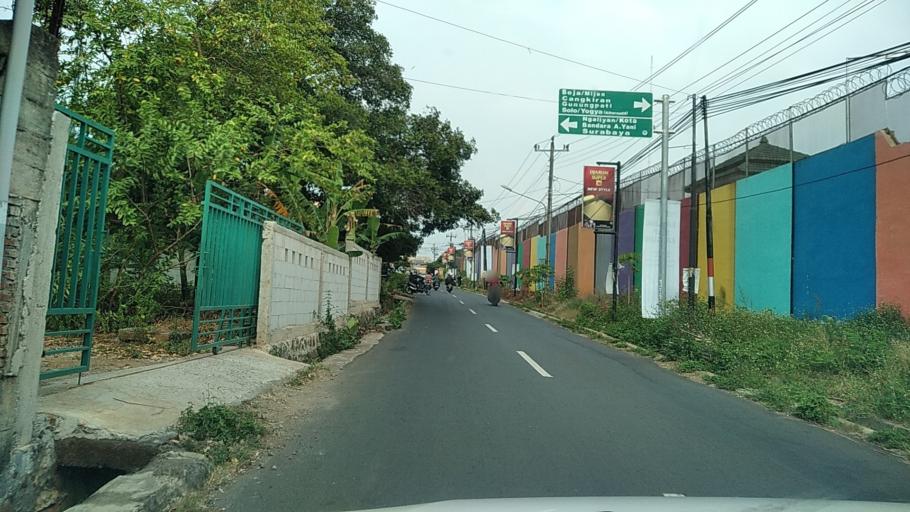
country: ID
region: Central Java
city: Semarang
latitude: -7.0135
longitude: 110.3364
